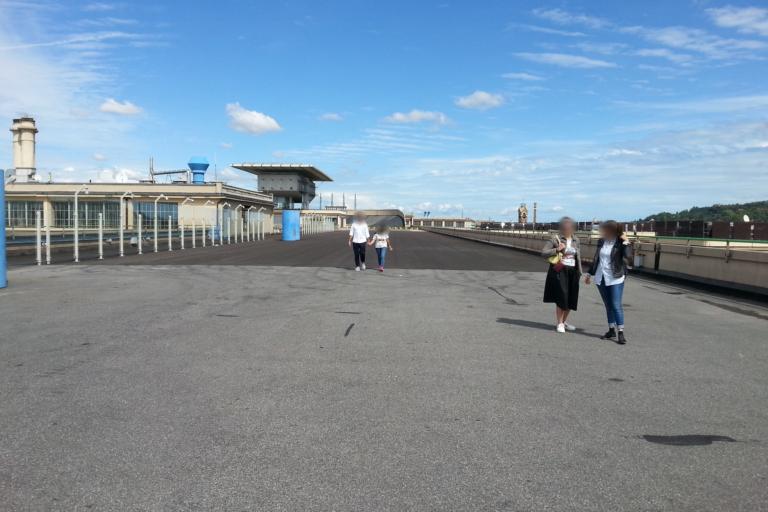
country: IT
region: Piedmont
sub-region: Provincia di Torino
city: Moncalieri
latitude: 45.0313
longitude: 7.6655
